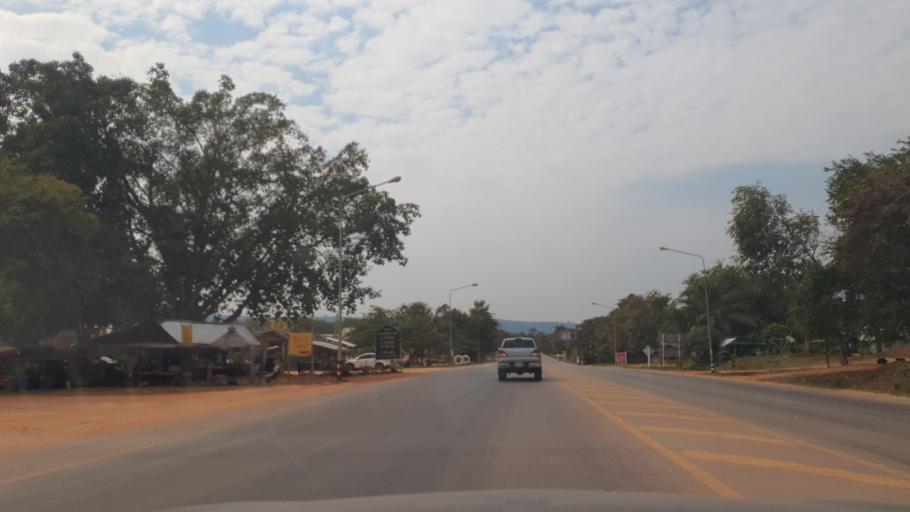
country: TH
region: Changwat Bueng Kan
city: Bung Khla
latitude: 18.2754
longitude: 103.8533
